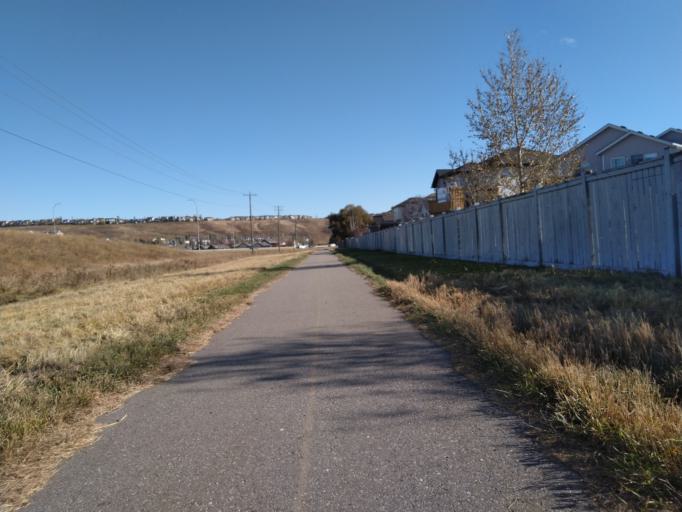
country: CA
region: Alberta
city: Calgary
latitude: 51.1541
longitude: -114.1109
